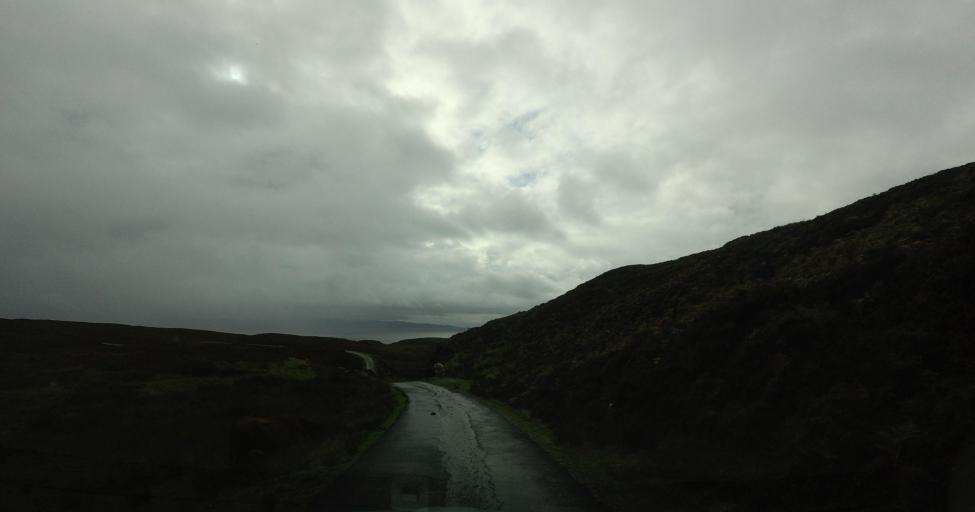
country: GB
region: Scotland
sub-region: Highland
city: Isle of Skye
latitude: 57.1443
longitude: -6.0907
